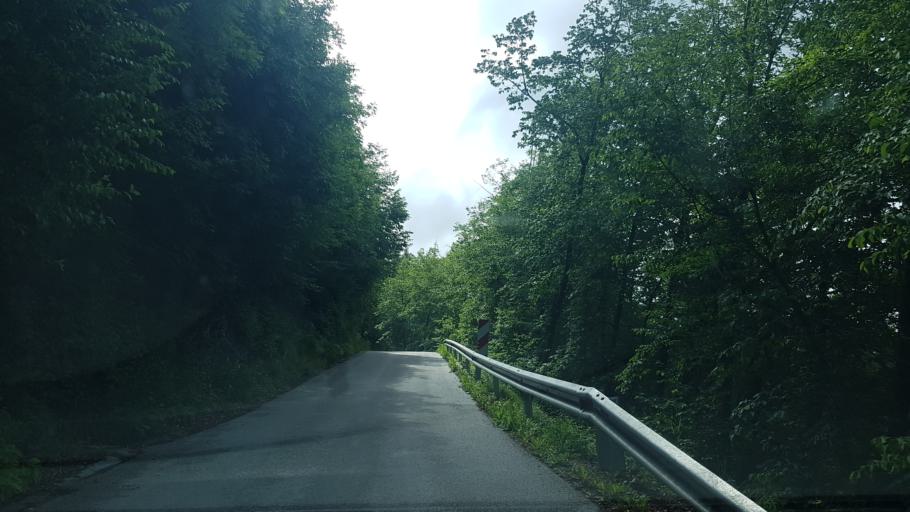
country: SI
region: Velenje
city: Velenje
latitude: 46.3899
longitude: 15.1754
